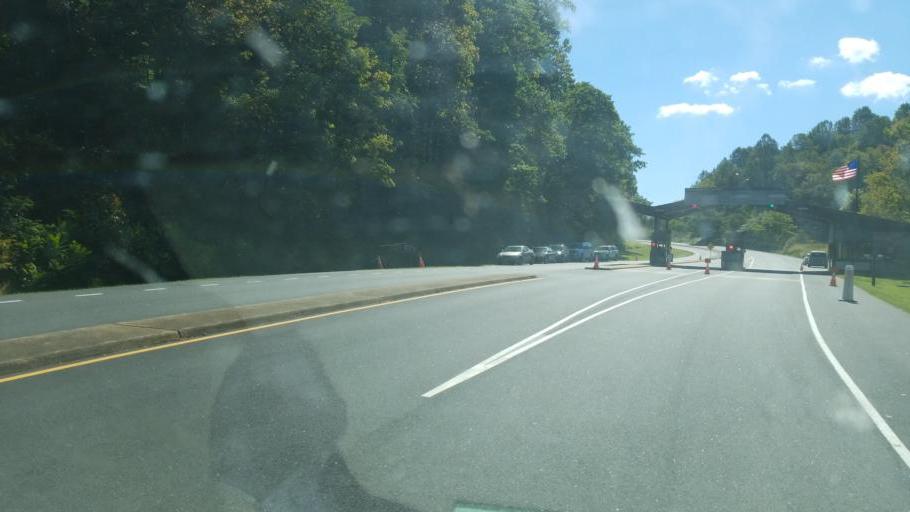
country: US
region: Virginia
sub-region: Rockingham County
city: Elkton
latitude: 38.3591
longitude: -78.5474
